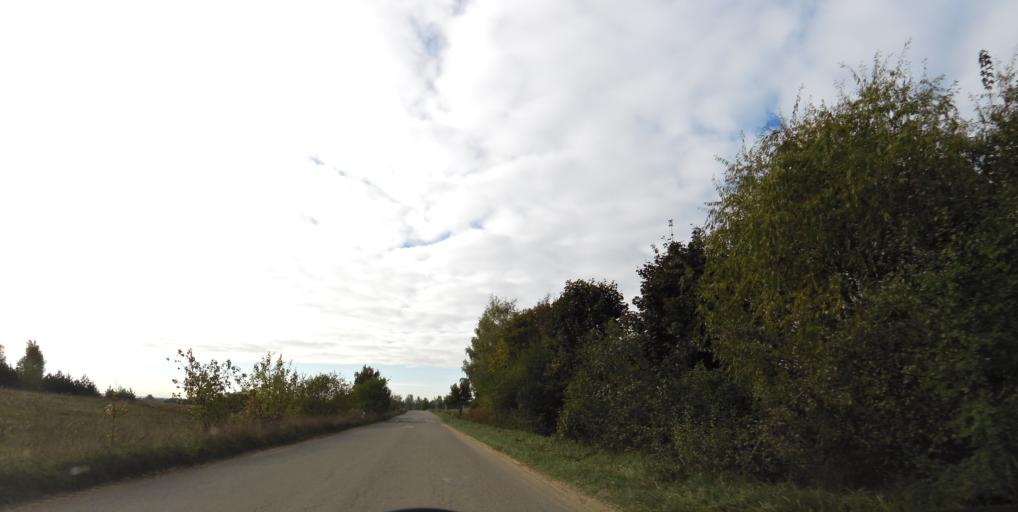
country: LT
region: Vilnius County
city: Pilaite
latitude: 54.7289
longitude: 25.1538
